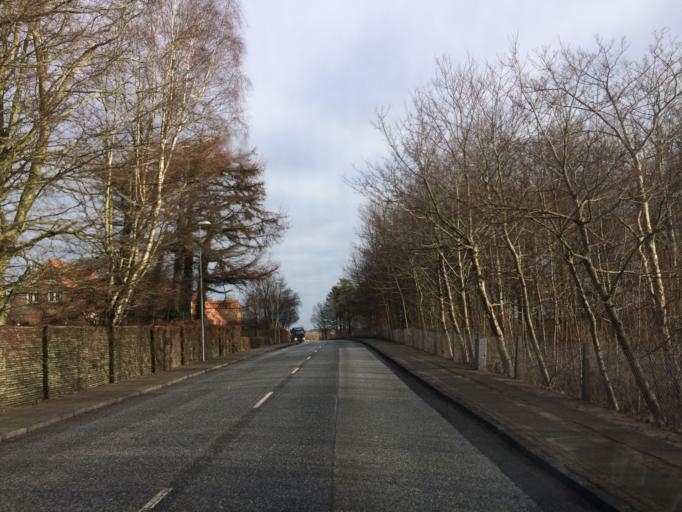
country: DK
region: Central Jutland
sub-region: Holstebro Kommune
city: Ulfborg
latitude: 56.3410
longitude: 8.3469
